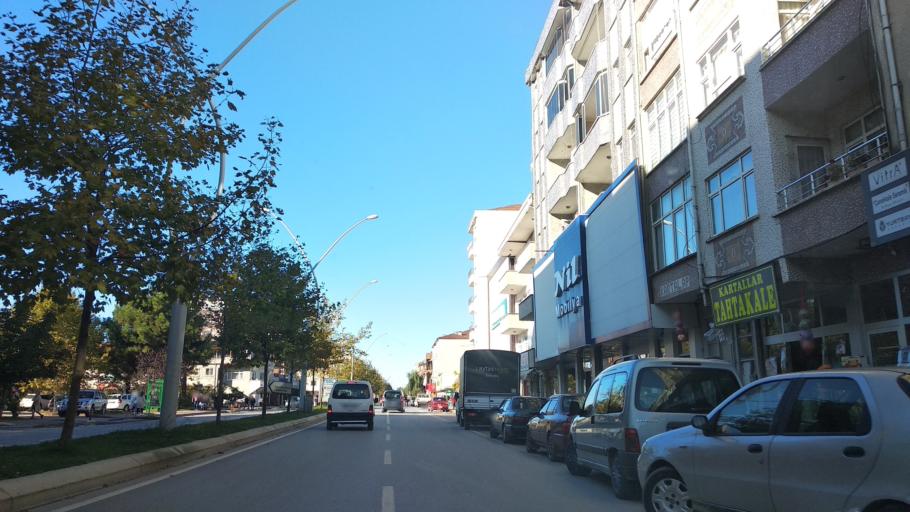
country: TR
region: Sakarya
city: Karasu
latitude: 41.0986
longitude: 30.6926
